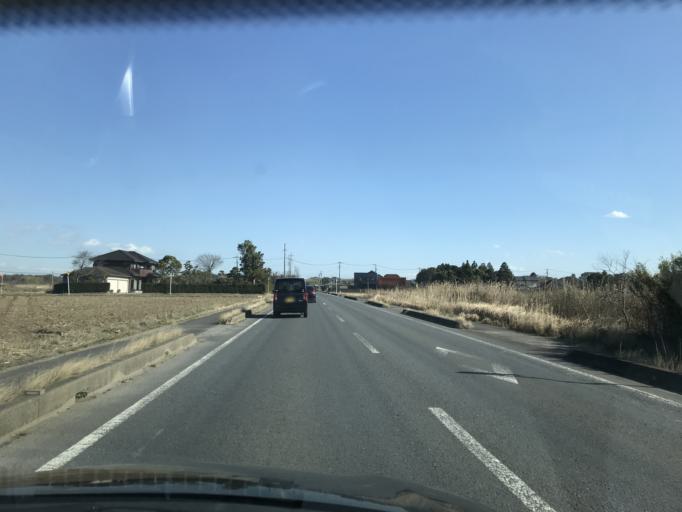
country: JP
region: Chiba
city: Omigawa
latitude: 35.8710
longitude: 140.6481
